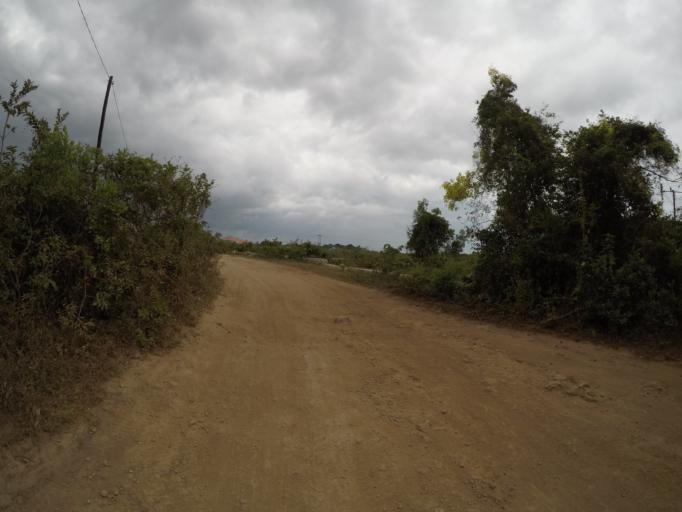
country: TZ
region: Zanzibar Central/South
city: Koani
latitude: -6.1939
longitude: 39.3082
